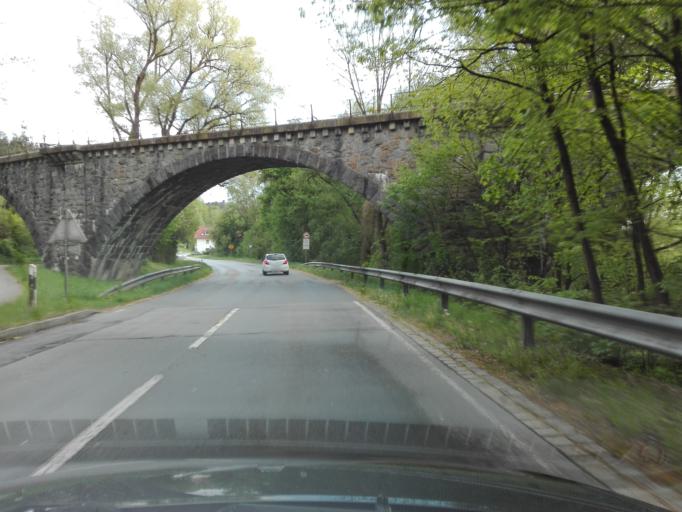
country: DE
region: Bavaria
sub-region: Lower Bavaria
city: Salzweg
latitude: 48.5800
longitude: 13.5032
